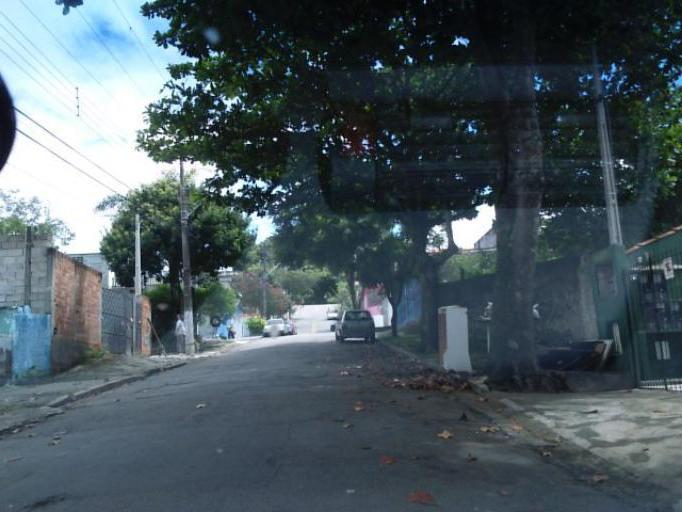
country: BR
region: Sao Paulo
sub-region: Sao Jose Dos Campos
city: Sao Jose dos Campos
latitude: -23.1981
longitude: -45.8629
